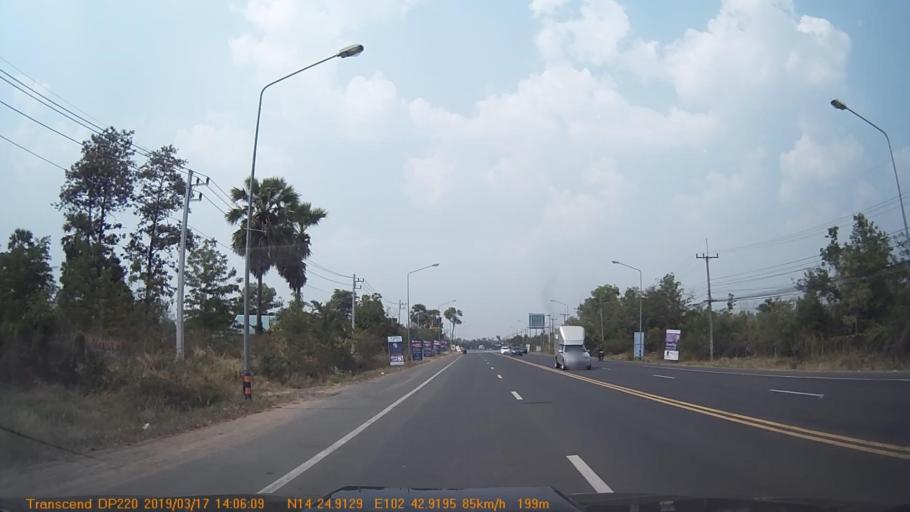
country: TH
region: Buriram
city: Pa Kham
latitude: 14.4155
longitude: 102.7153
